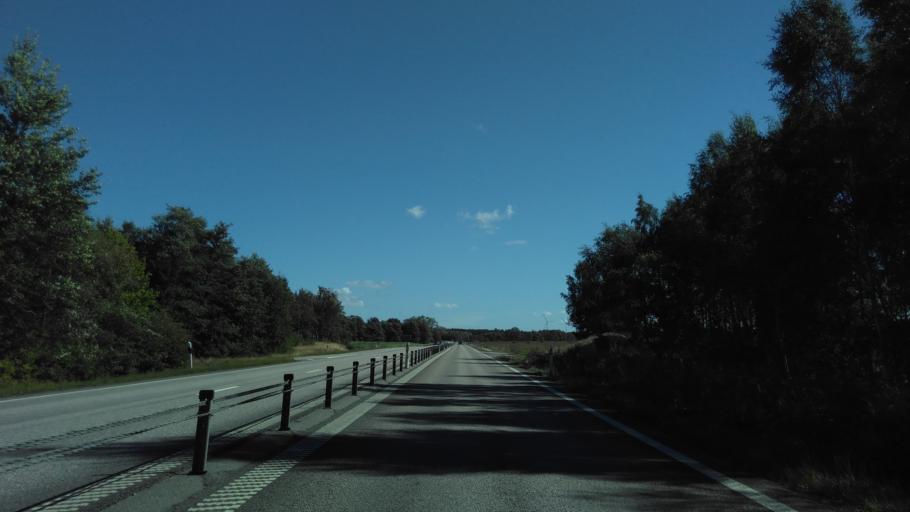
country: SE
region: Vaestra Goetaland
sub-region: Vara Kommun
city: Kvanum
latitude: 58.3497
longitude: 13.2688
